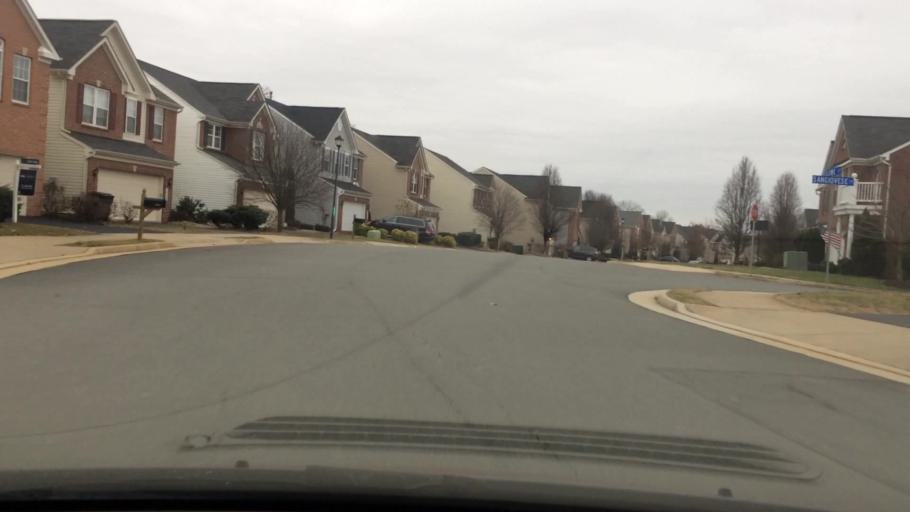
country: US
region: Virginia
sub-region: Fairfax County
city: Chantilly
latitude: 38.9012
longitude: -77.4234
